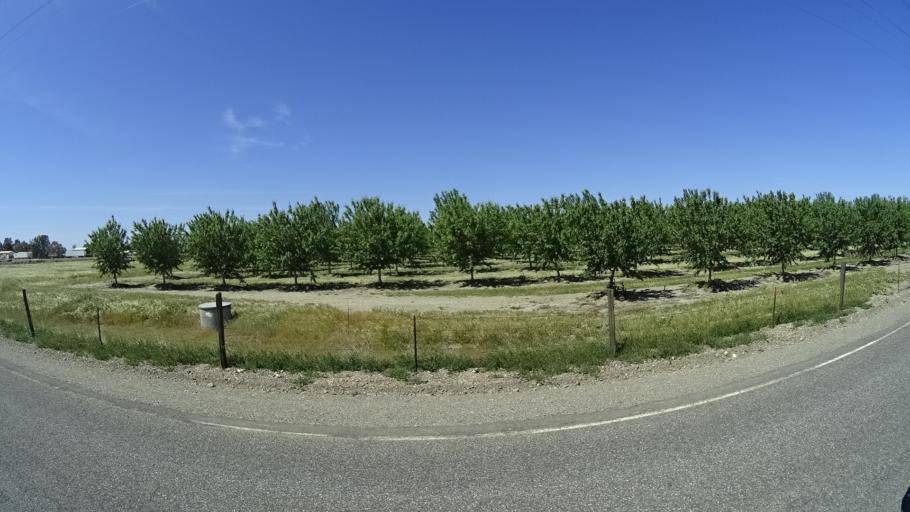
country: US
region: California
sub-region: Glenn County
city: Orland
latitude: 39.6710
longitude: -122.1783
